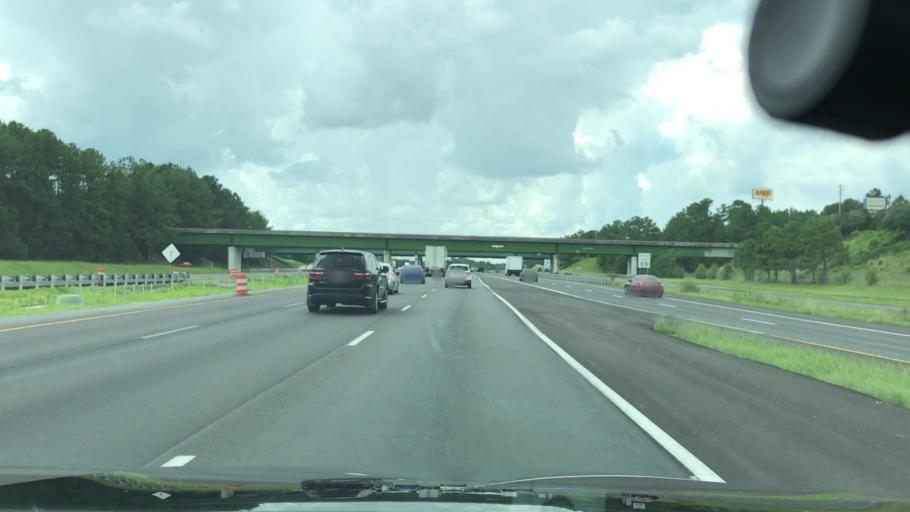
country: US
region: South Carolina
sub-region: Richland County
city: Dentsville
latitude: 34.0976
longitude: -80.9567
